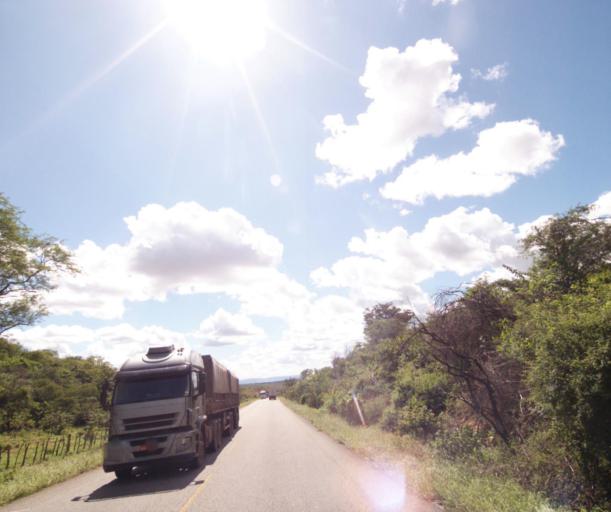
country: BR
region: Bahia
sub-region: Caetite
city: Caetite
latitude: -14.1719
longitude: -42.2165
